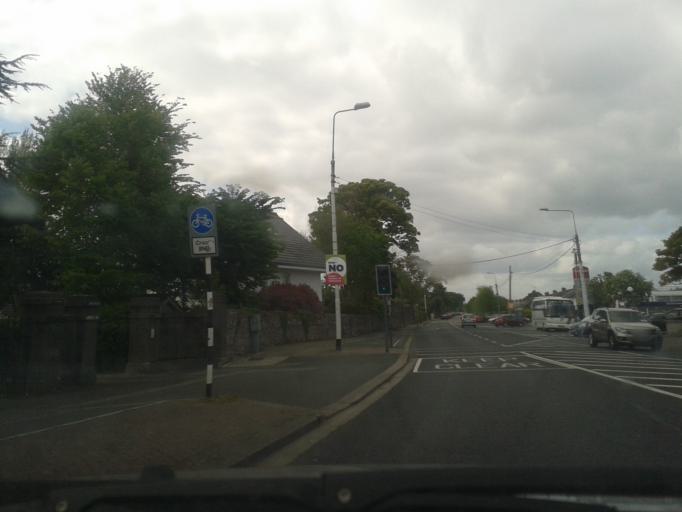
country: IE
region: Leinster
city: Sallynoggin
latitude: 53.2665
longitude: -6.1355
